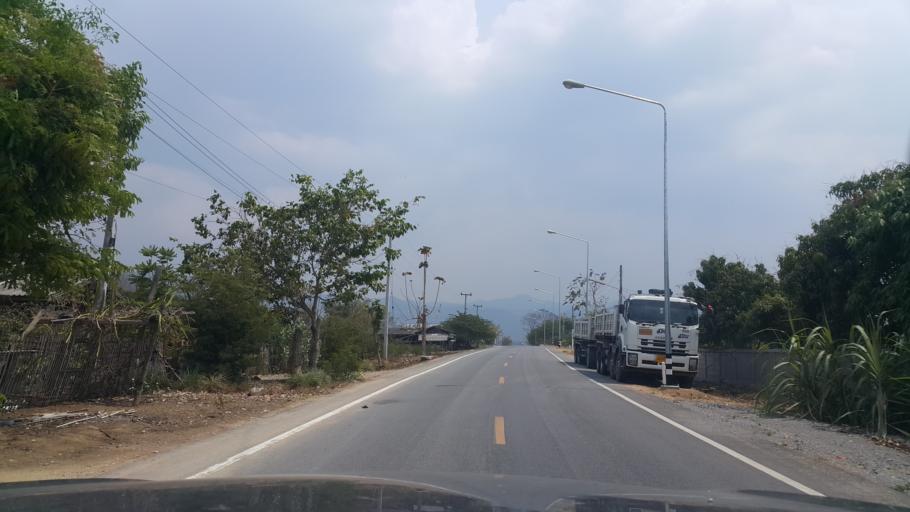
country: TH
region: Lamphun
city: Ban Hong
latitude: 18.2660
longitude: 98.9287
